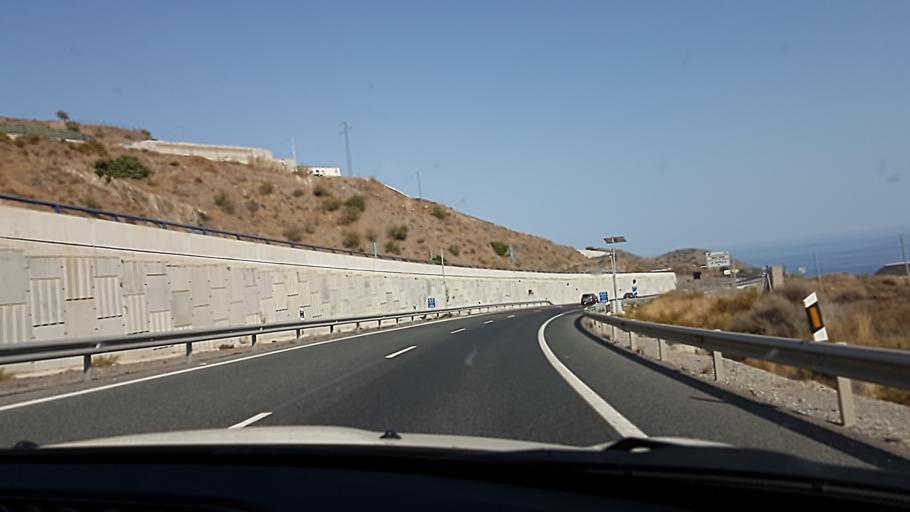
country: ES
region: Andalusia
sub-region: Provincia de Granada
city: Polopos
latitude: 36.7513
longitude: -3.3202
